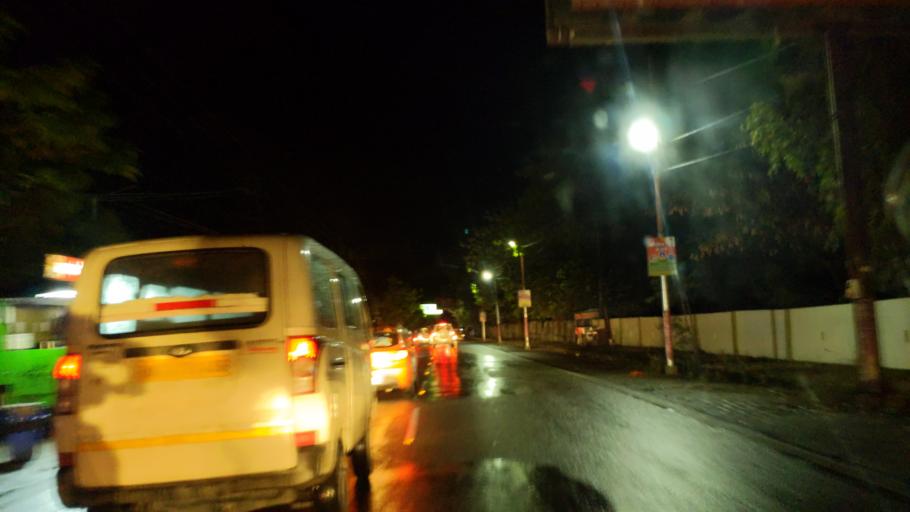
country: IN
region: Uttarakhand
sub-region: Naini Tal
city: Haldwani
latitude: 29.2068
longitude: 79.5201
